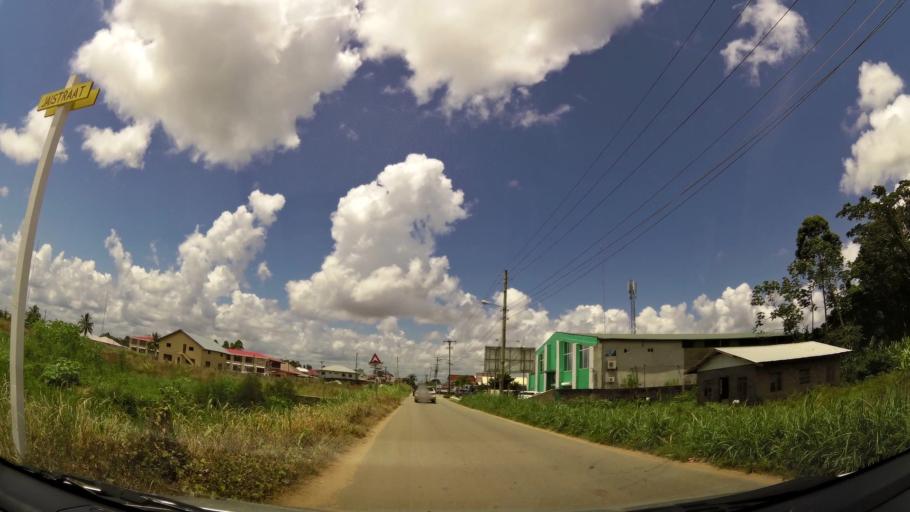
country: SR
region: Paramaribo
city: Paramaribo
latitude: 5.8577
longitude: -55.1665
